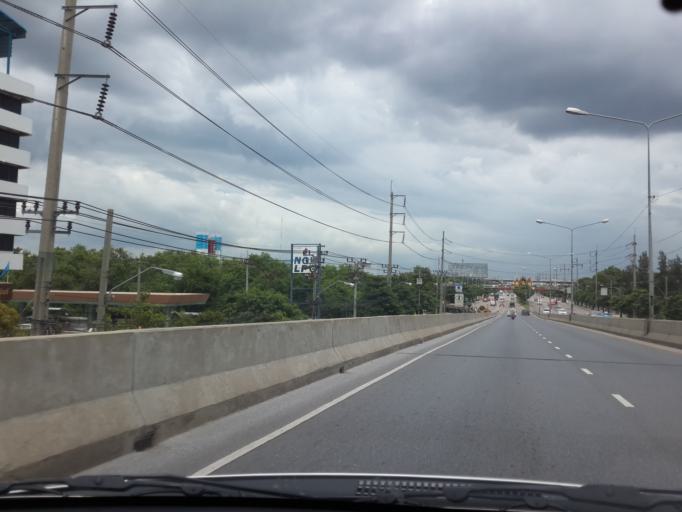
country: TH
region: Bangkok
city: Min Buri
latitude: 13.8131
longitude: 100.7381
